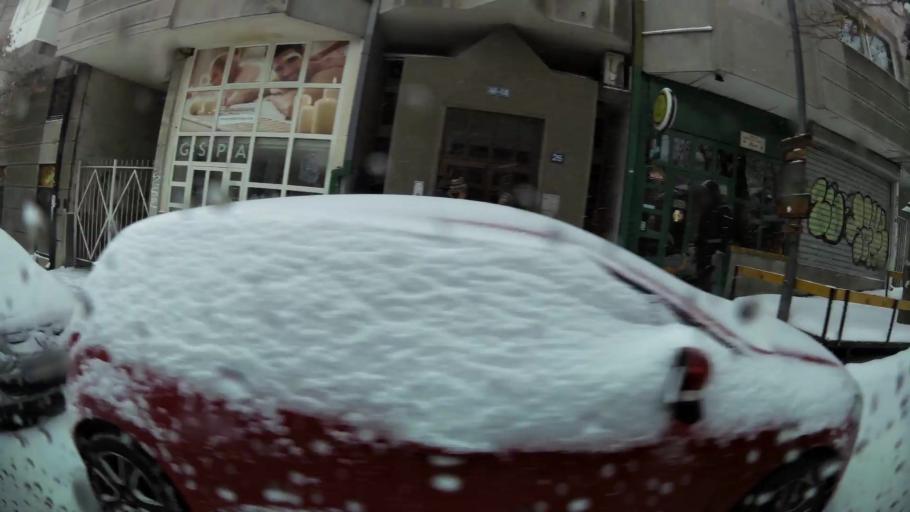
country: RS
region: Central Serbia
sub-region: Belgrade
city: Stari Grad
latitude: 44.8207
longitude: 20.4626
